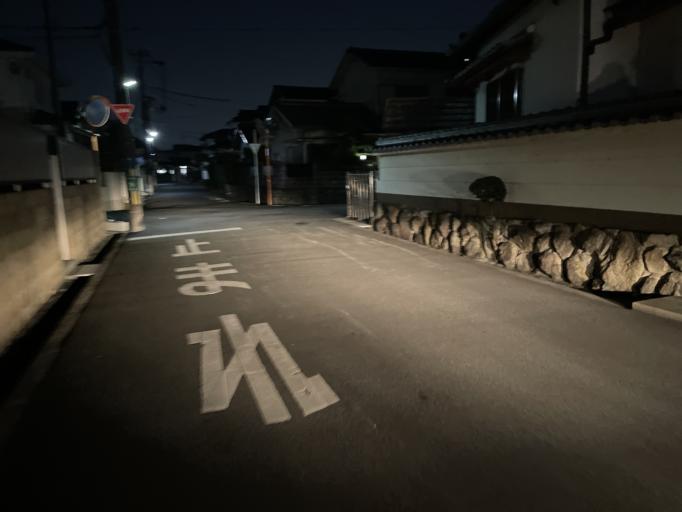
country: JP
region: Osaka
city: Ibaraki
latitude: 34.8047
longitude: 135.5817
